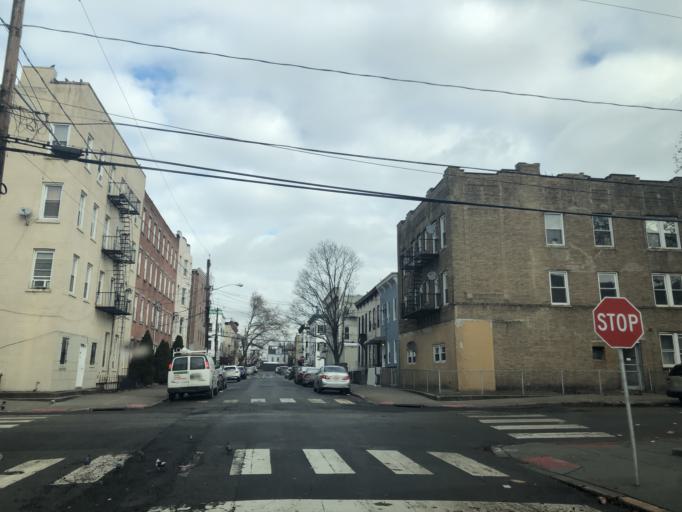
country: US
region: New Jersey
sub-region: Hudson County
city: Hoboken
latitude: 40.7332
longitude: -74.0526
